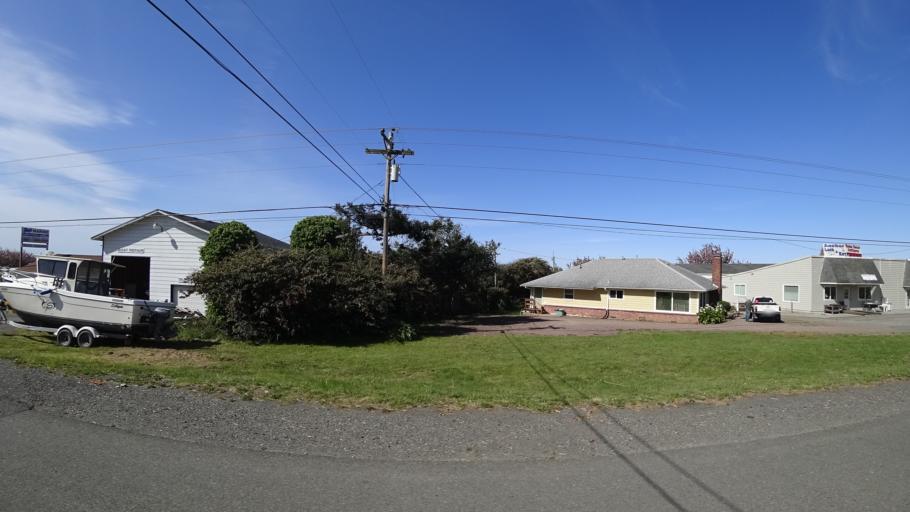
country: US
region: Oregon
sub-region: Curry County
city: Harbor
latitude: 42.0353
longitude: -124.2418
